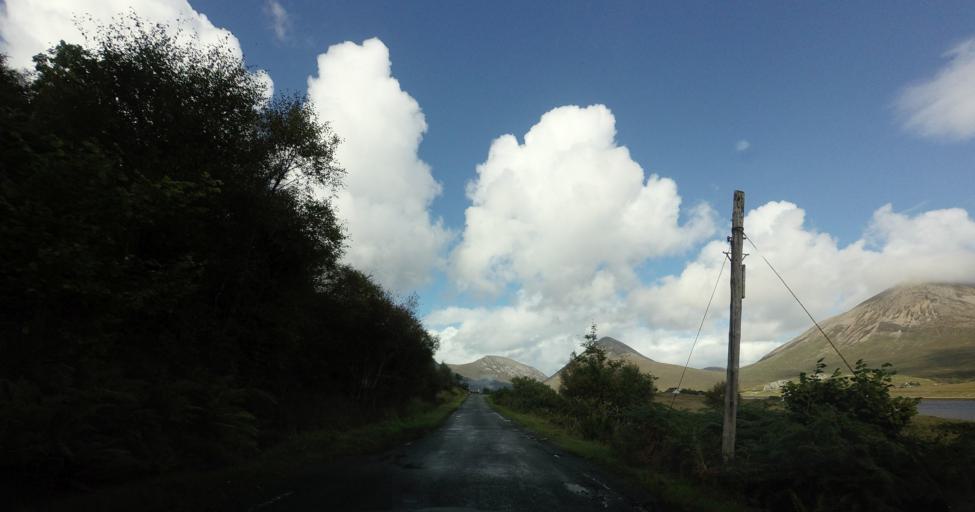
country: GB
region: Scotland
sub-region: Highland
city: Portree
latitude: 57.2055
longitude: -6.0283
